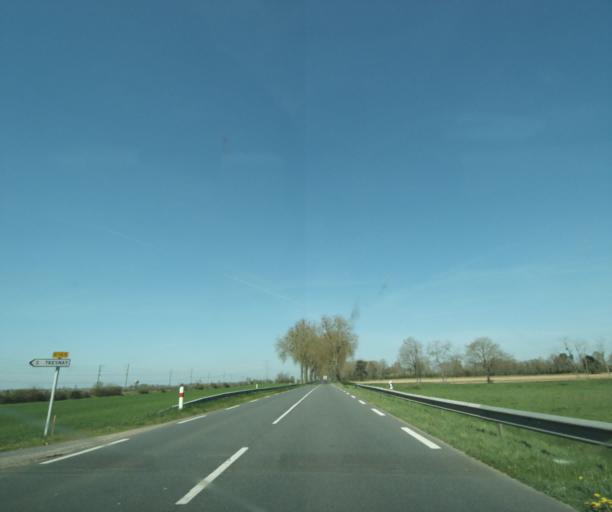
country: FR
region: Bourgogne
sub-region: Departement de la Nievre
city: Chantenay-Saint-Imbert
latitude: 46.6854
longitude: 3.2219
